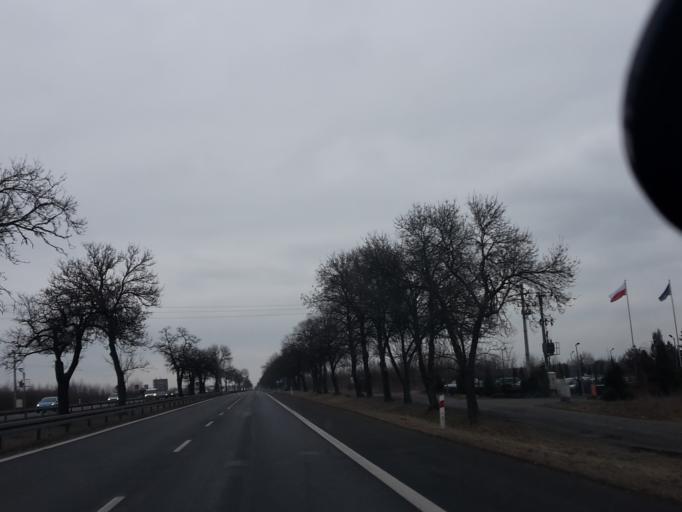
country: PL
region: Masovian Voivodeship
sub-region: Powiat nowodworski
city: Nowy Dwor Mazowiecki
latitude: 52.3801
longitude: 20.7647
